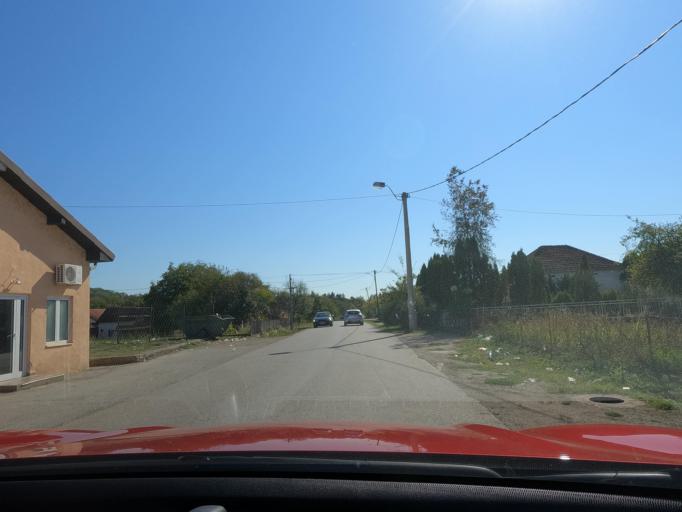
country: RS
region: Central Serbia
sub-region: Raski Okrug
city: Kraljevo
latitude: 43.7615
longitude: 20.6775
